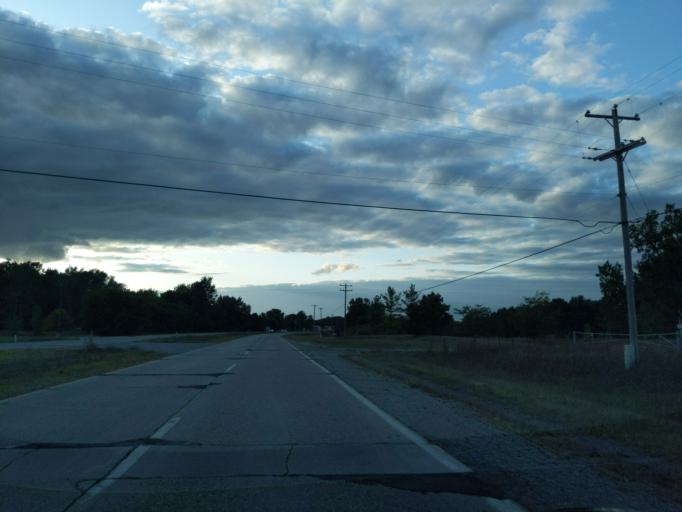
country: US
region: Michigan
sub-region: Ingham County
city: Holt
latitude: 42.6137
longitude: -84.4935
